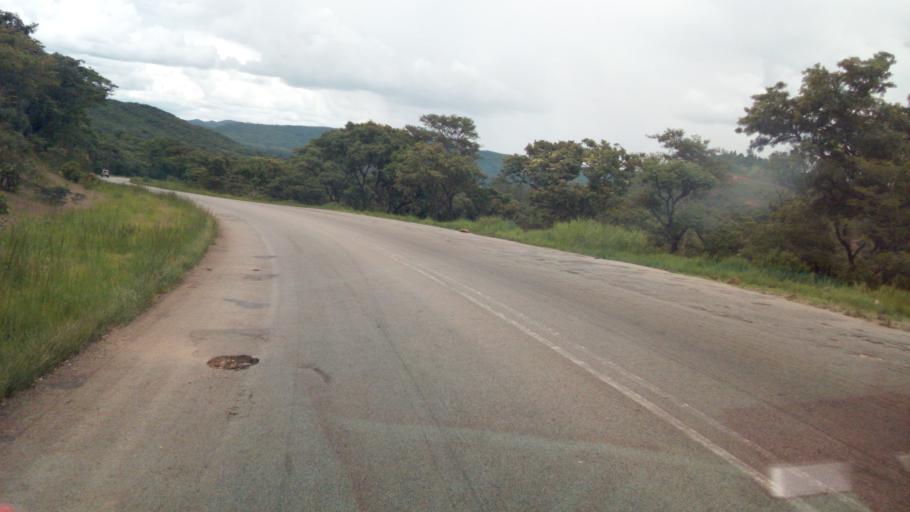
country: ZW
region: Mashonaland Central
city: Mazowe
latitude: -17.6326
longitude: 30.9747
